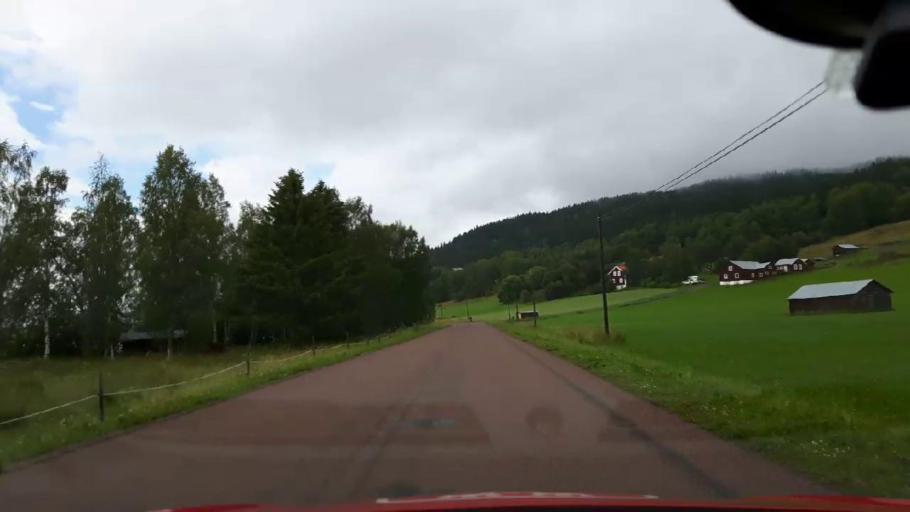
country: SE
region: Jaemtland
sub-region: Krokoms Kommun
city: Valla
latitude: 63.3805
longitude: 14.0111
